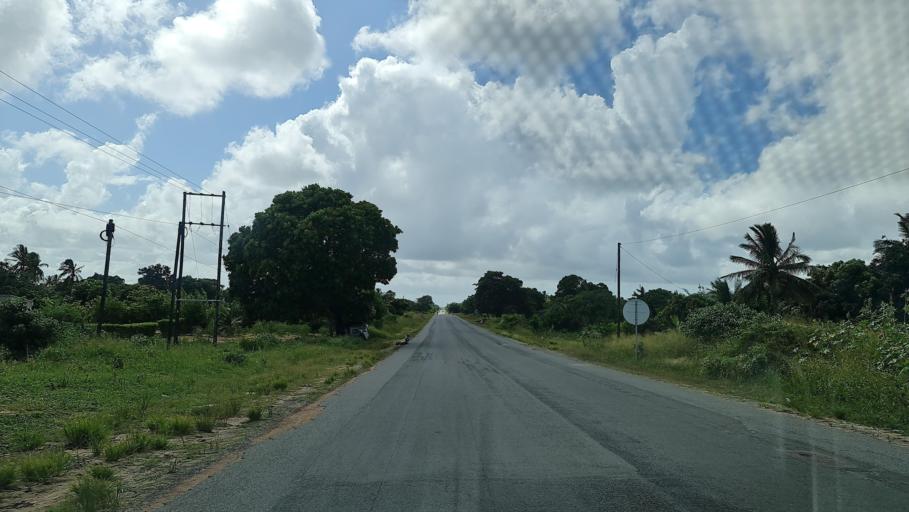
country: MZ
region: Gaza
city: Manjacaze
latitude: -24.6758
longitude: 34.5850
